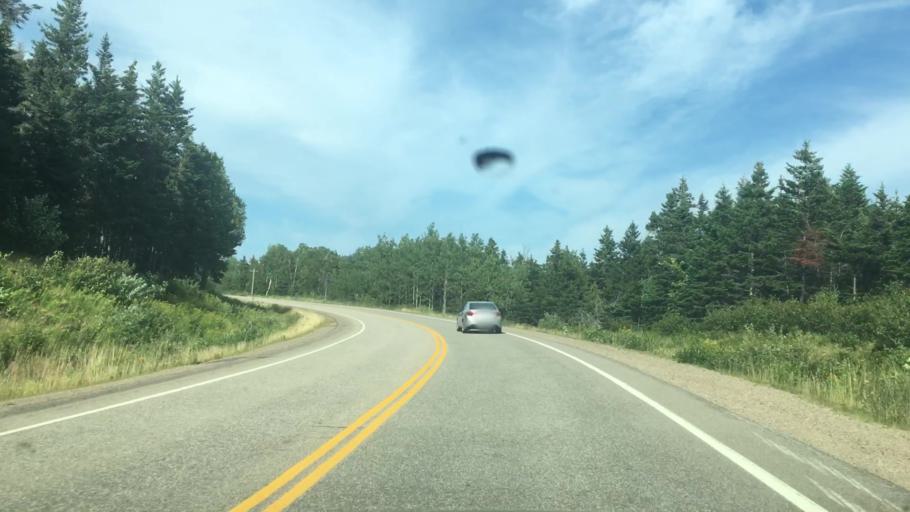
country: CA
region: Nova Scotia
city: Sydney Mines
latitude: 46.7145
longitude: -60.3534
